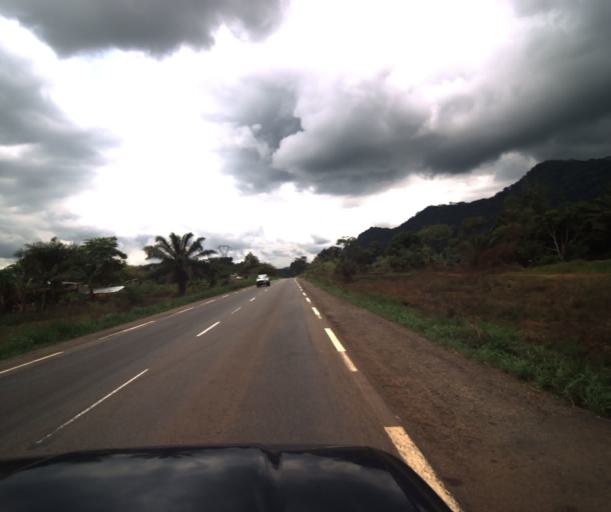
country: CM
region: Centre
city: Eseka
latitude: 3.8918
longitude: 10.7730
